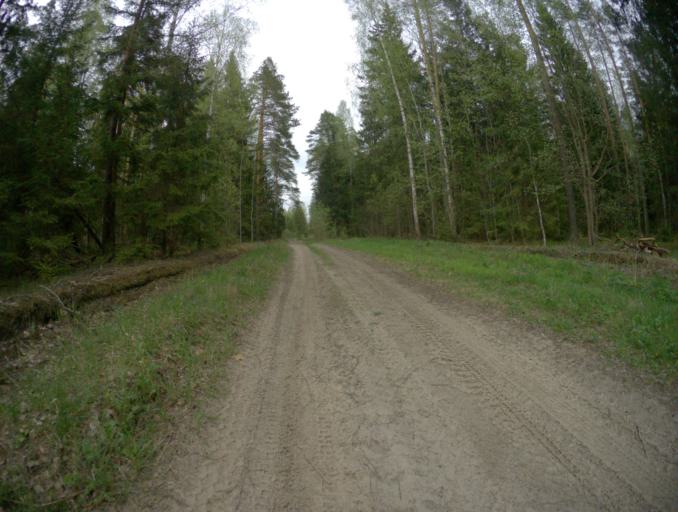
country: RU
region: Vladimir
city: Golovino
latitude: 55.8991
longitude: 40.4284
